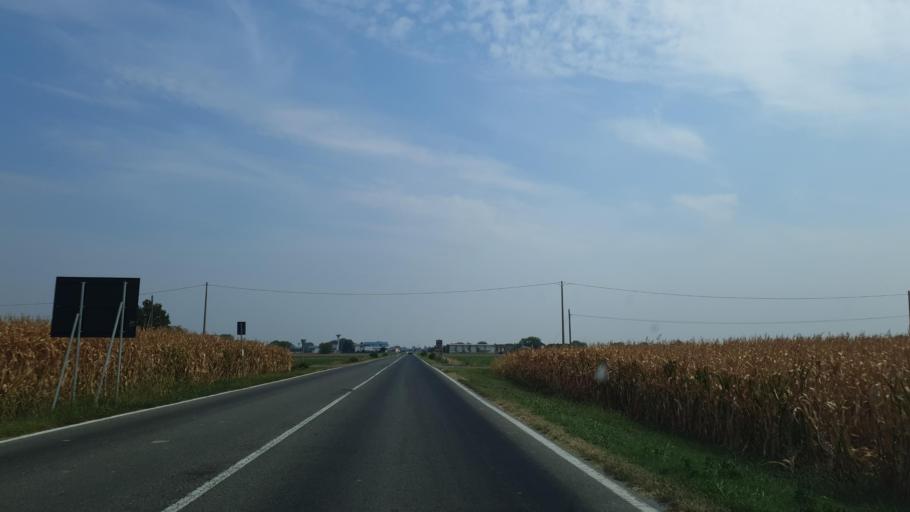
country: IT
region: Emilia-Romagna
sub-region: Provincia di Parma
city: Roccabianca
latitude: 45.0079
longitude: 10.1807
